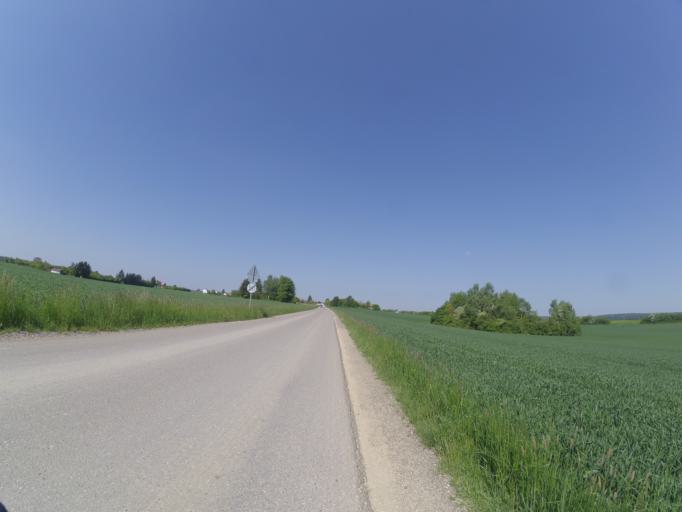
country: DE
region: Baden-Wuerttemberg
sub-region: Tuebingen Region
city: Dornstadt
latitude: 48.4603
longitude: 9.8582
